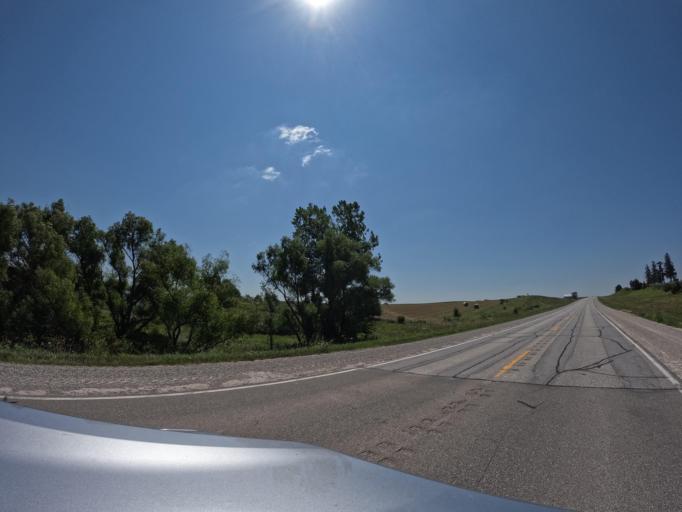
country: US
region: Iowa
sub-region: Keokuk County
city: Sigourney
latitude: 41.2799
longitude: -92.2044
